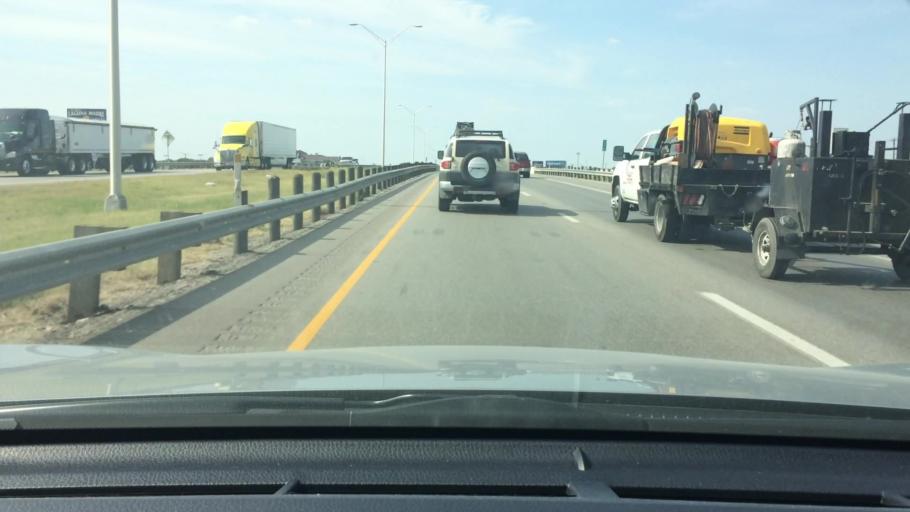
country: US
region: Texas
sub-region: Bexar County
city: China Grove
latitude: 29.3969
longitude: -98.3892
